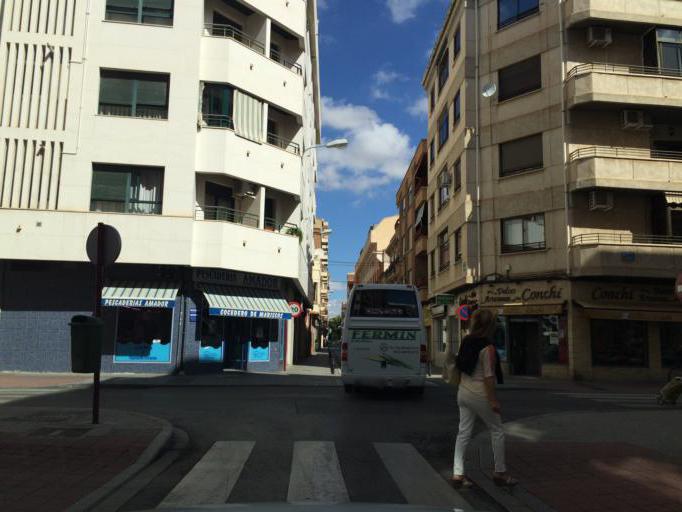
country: ES
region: Castille-La Mancha
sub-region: Provincia de Albacete
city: Albacete
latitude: 38.9978
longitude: -1.8572
